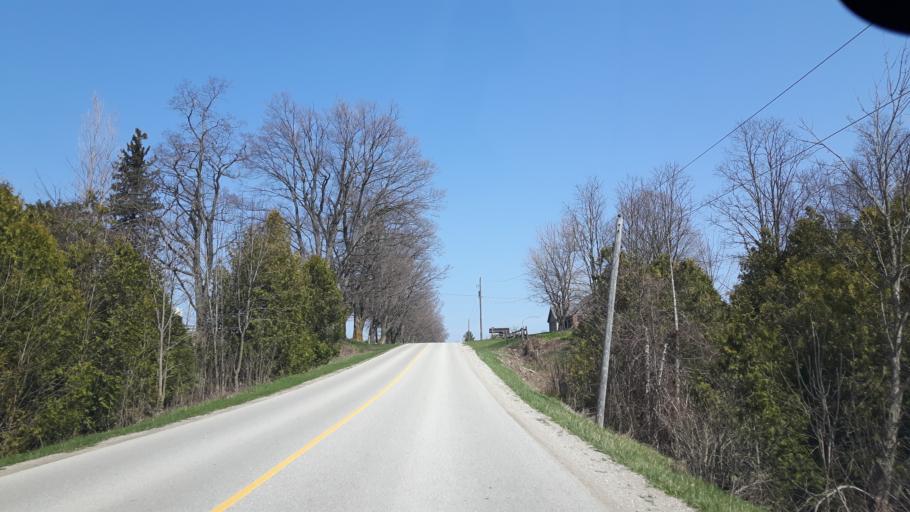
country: CA
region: Ontario
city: Goderich
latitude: 43.6685
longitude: -81.6846
